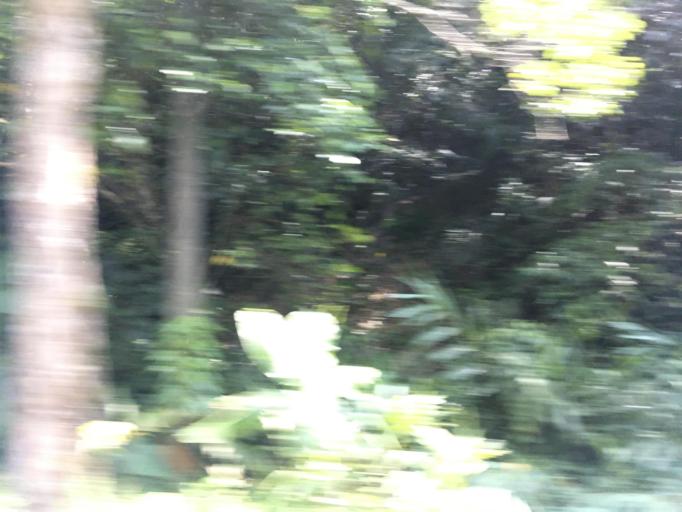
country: TW
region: Taiwan
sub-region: Yilan
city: Yilan
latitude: 24.8163
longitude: 121.7349
